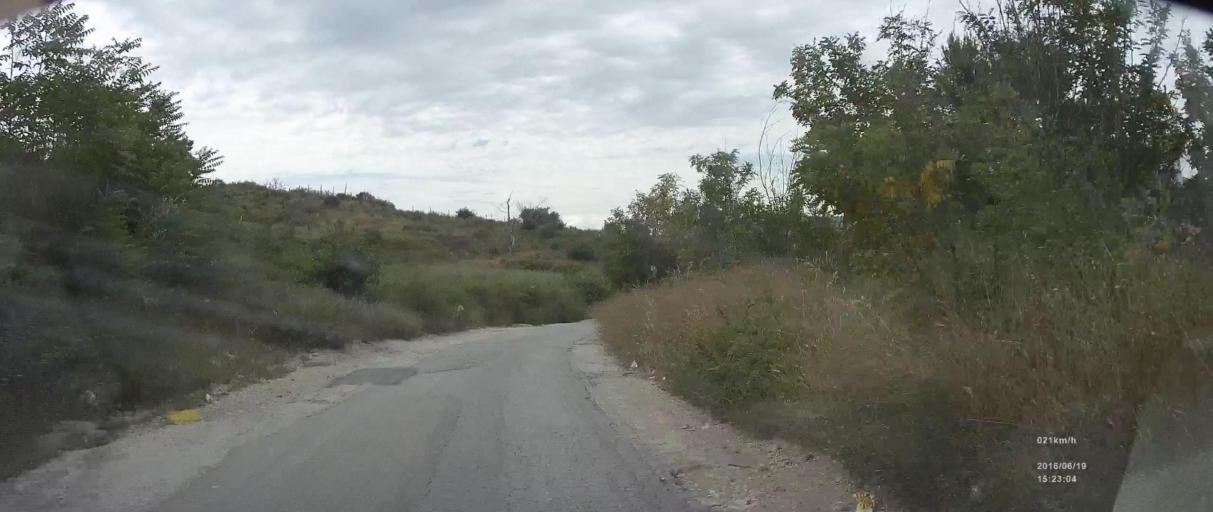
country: HR
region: Splitsko-Dalmatinska
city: Kamen
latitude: 43.5124
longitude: 16.5011
